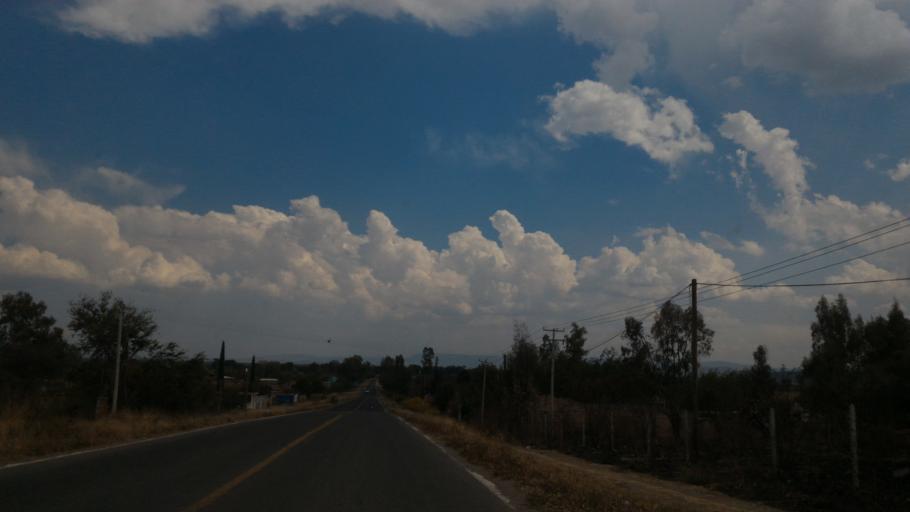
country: MX
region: Guanajuato
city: Ciudad Manuel Doblado
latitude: 20.8026
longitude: -101.9927
